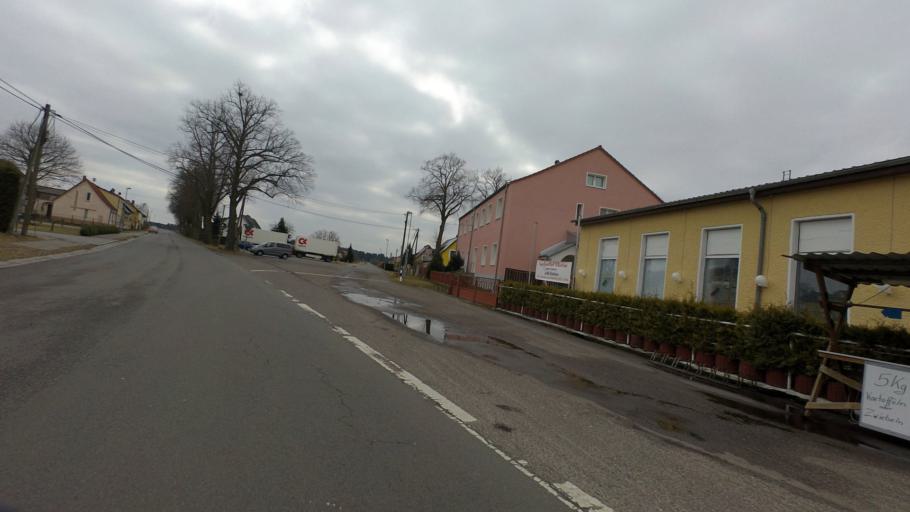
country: DE
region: Brandenburg
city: Trebbin
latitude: 52.2004
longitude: 13.2090
